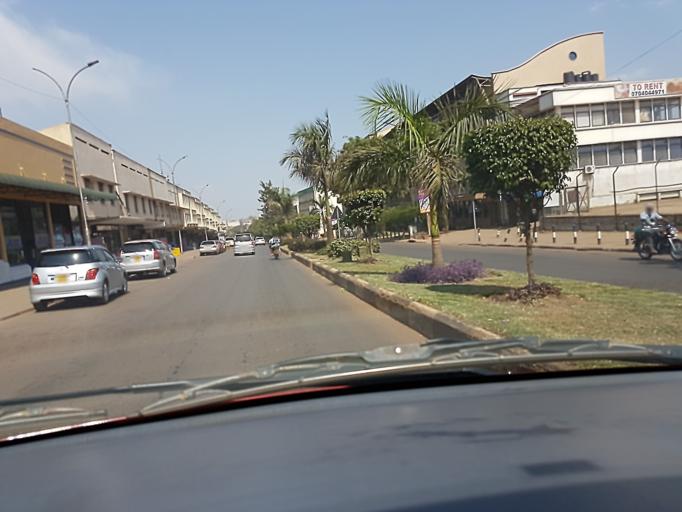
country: UG
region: Central Region
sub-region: Kampala District
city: Kampala
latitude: 0.3141
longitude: 32.5894
